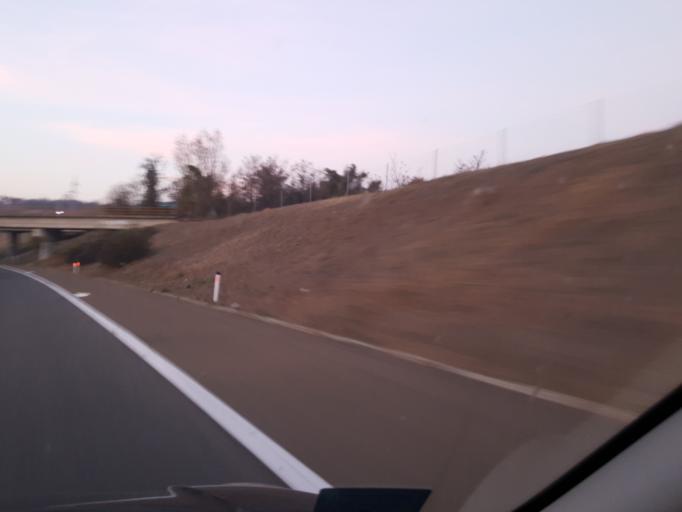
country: RS
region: Central Serbia
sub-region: Pomoravski Okrug
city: Paracin
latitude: 43.8642
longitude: 21.4361
